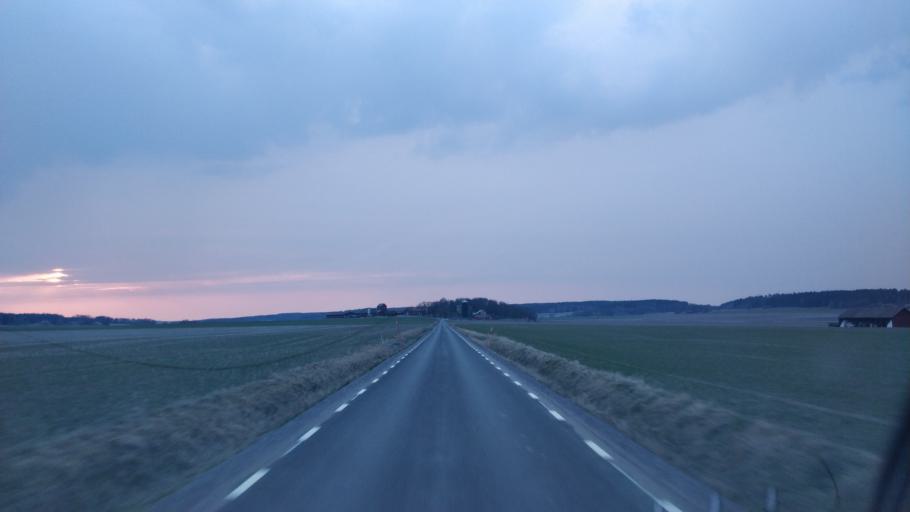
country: SE
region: Uppsala
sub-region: Enkopings Kommun
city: Orsundsbro
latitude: 59.7343
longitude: 17.1943
